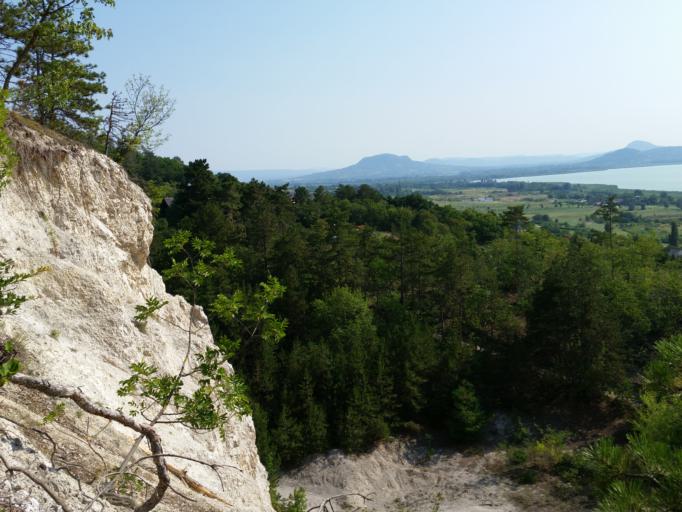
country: HU
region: Zala
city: Vonyarcvashegy
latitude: 46.7710
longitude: 17.3574
